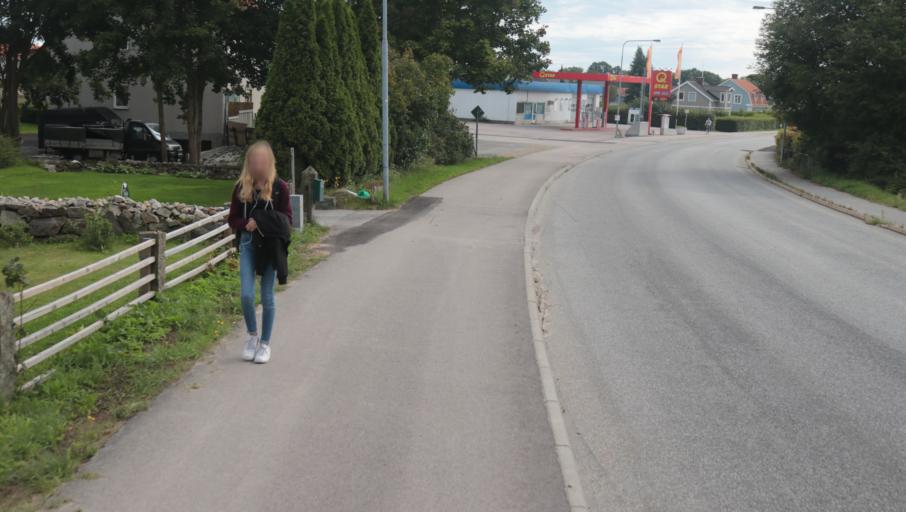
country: SE
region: Blekinge
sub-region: Karlshamns Kommun
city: Karlshamn
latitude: 56.2179
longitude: 14.8326
